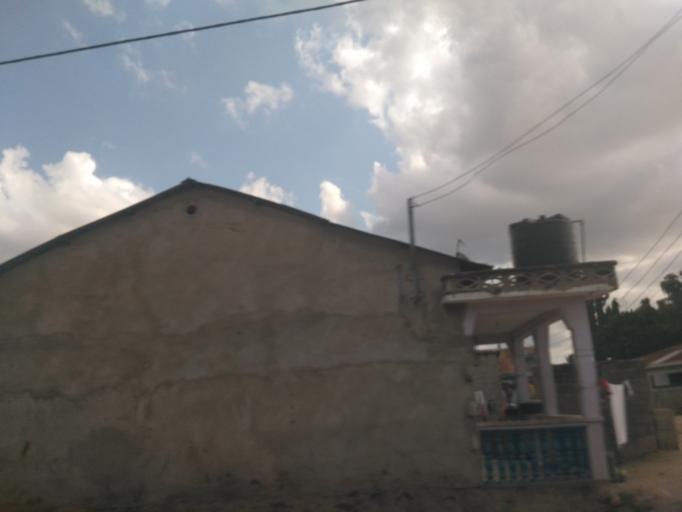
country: TZ
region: Dar es Salaam
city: Dar es Salaam
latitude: -6.8960
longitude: 39.2799
